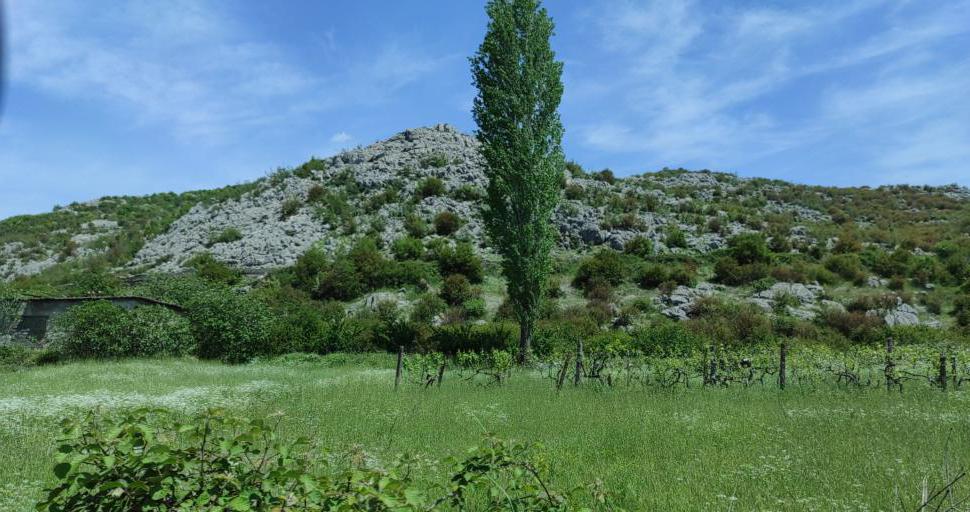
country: AL
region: Shkoder
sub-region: Rrethi i Malesia e Madhe
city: Gruemire
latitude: 42.1451
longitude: 19.5449
